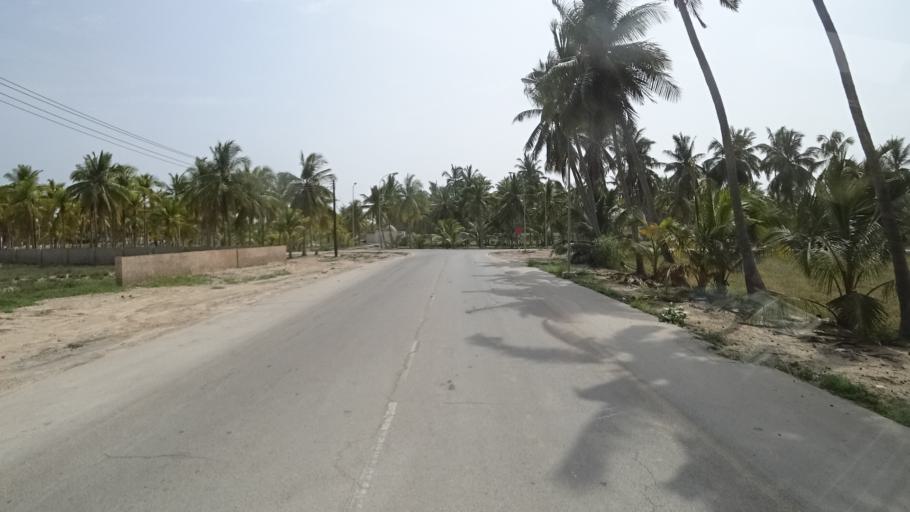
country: OM
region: Zufar
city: Salalah
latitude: 17.0111
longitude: 54.1540
